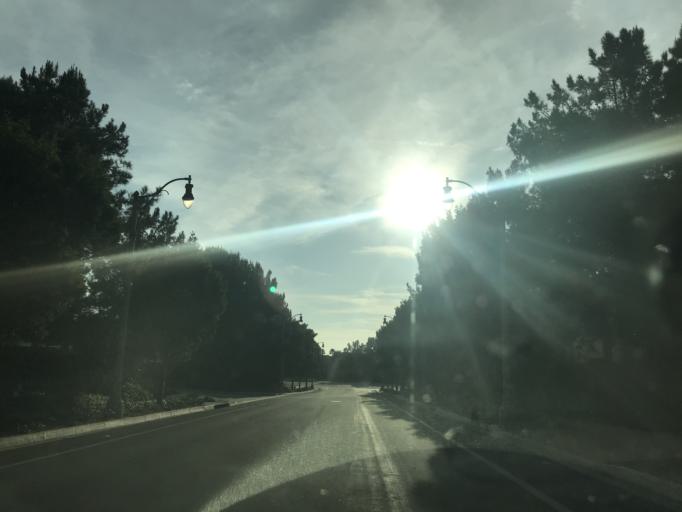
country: US
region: California
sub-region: Orange County
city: Lake Forest
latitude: 33.7000
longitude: -117.7432
